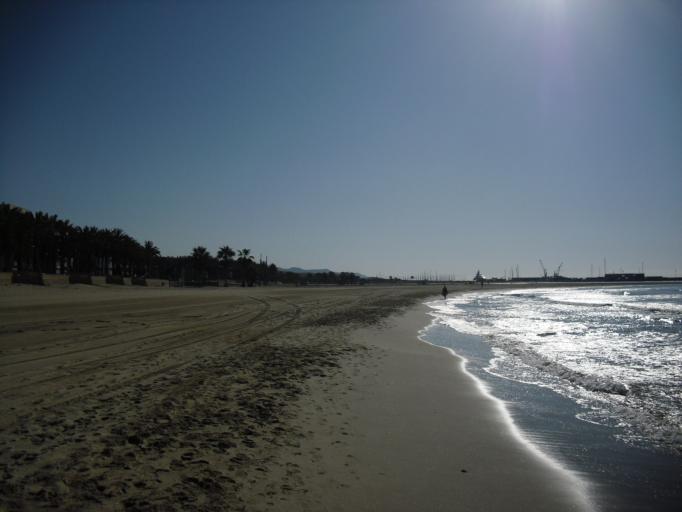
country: ES
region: Catalonia
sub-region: Provincia de Barcelona
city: Vilanova i la Geltru
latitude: 41.2113
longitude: 1.7157
